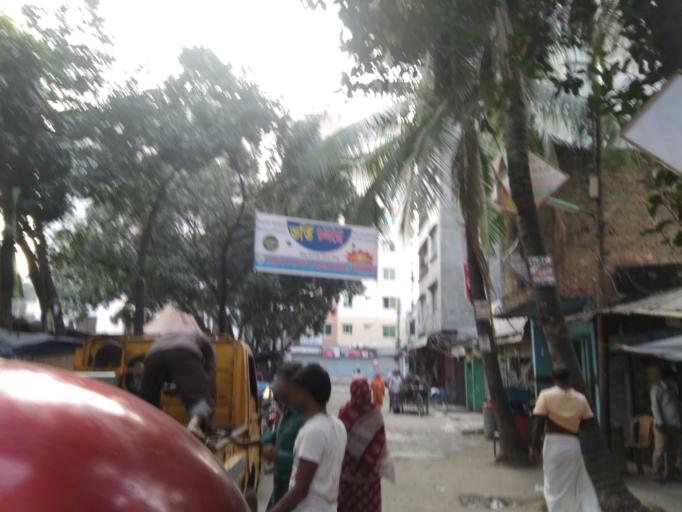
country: BD
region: Dhaka
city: Azimpur
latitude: 23.8111
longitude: 90.3633
